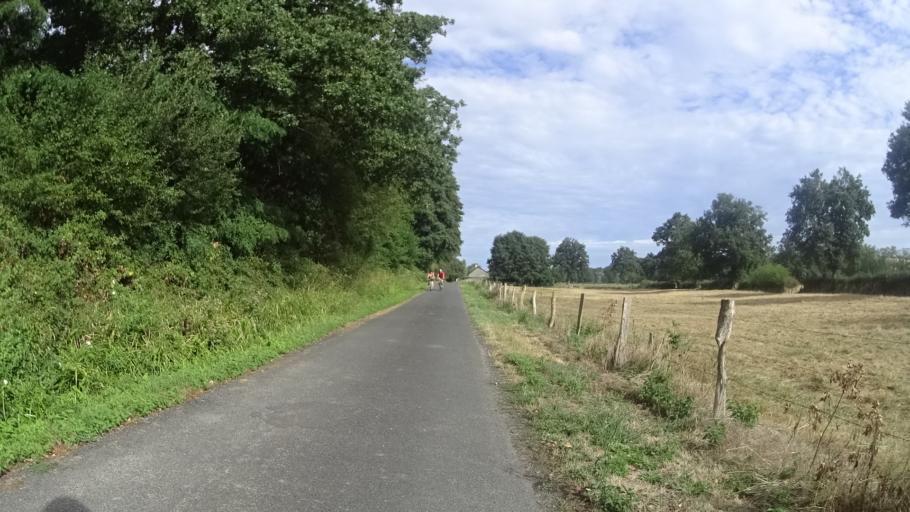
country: FR
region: Auvergne
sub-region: Departement de l'Allier
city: Diou
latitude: 46.5276
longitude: 3.7733
